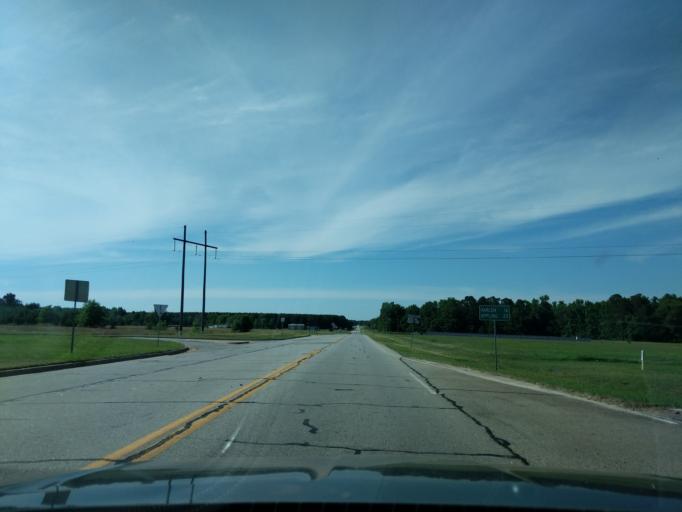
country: US
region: Georgia
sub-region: Jefferson County
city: Wrens
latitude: 33.2195
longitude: -82.3775
